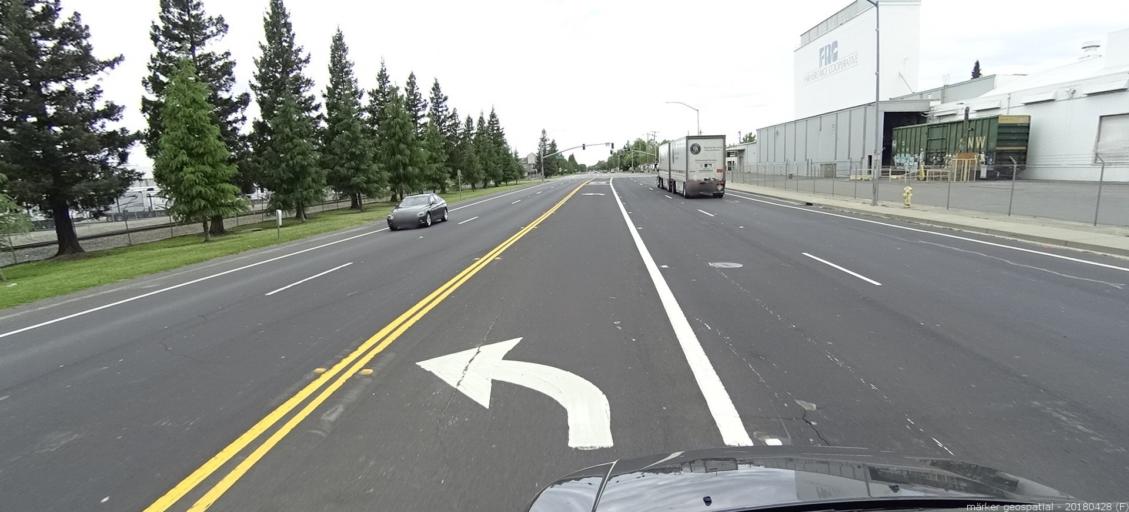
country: US
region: California
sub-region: Yolo County
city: West Sacramento
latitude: 38.5644
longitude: -121.5420
